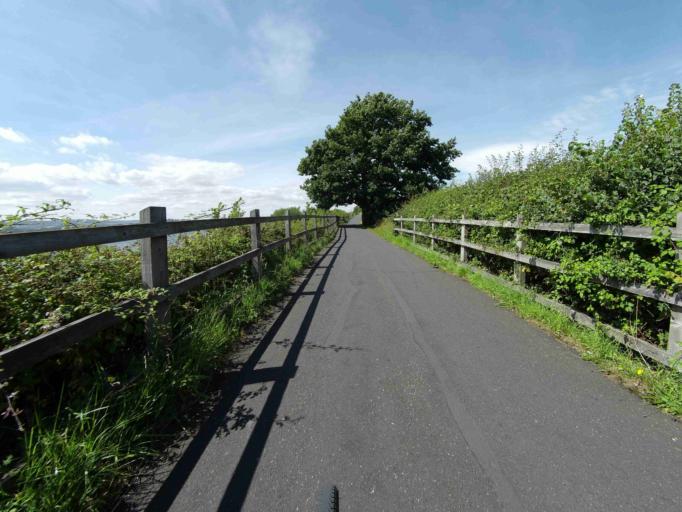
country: GB
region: England
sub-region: Devon
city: Starcross
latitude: 50.6407
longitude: -3.4246
